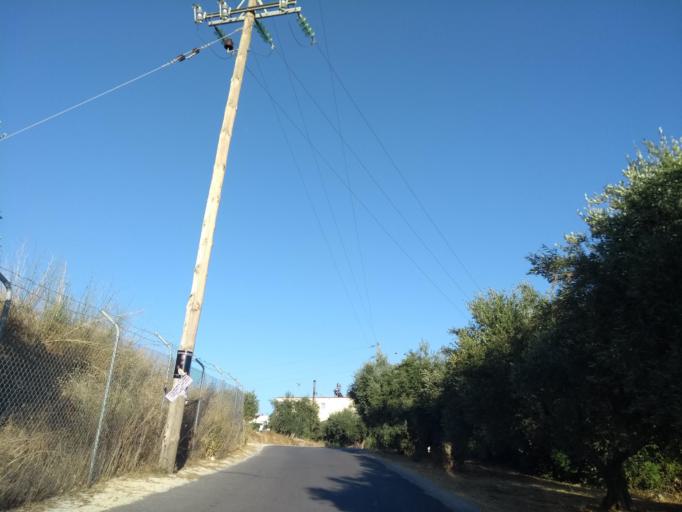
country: GR
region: Crete
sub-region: Nomos Chanias
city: Kalivai
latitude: 35.4362
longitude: 24.1741
